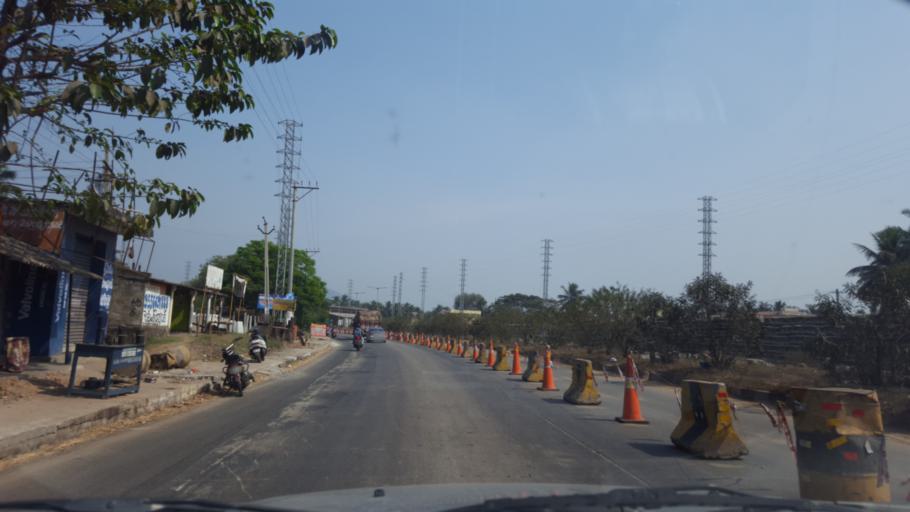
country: IN
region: Andhra Pradesh
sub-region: Vishakhapatnam
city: Anakapalle
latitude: 17.6749
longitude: 82.9983
